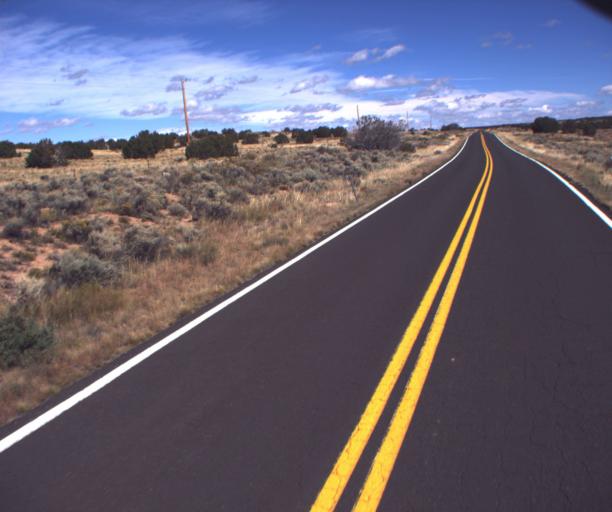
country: US
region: Arizona
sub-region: Apache County
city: Houck
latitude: 34.9428
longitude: -109.1771
